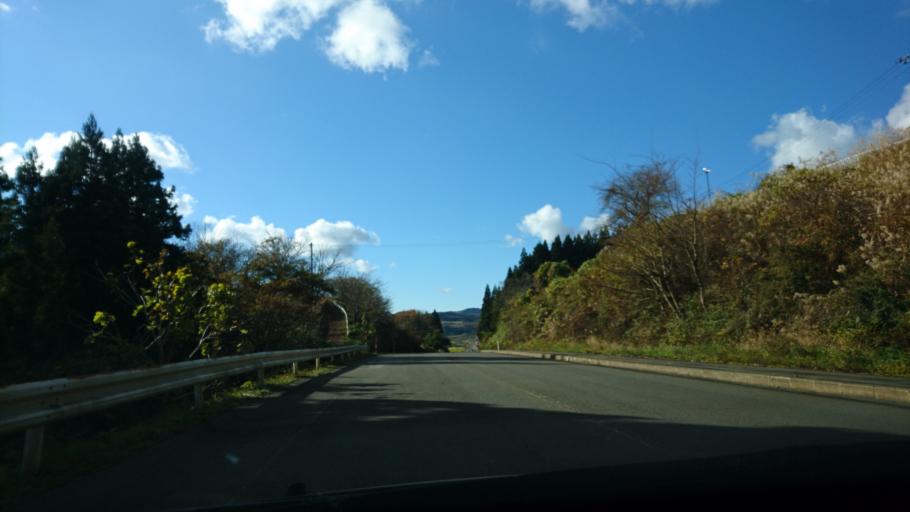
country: JP
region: Akita
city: Omagari
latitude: 39.3072
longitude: 140.2483
